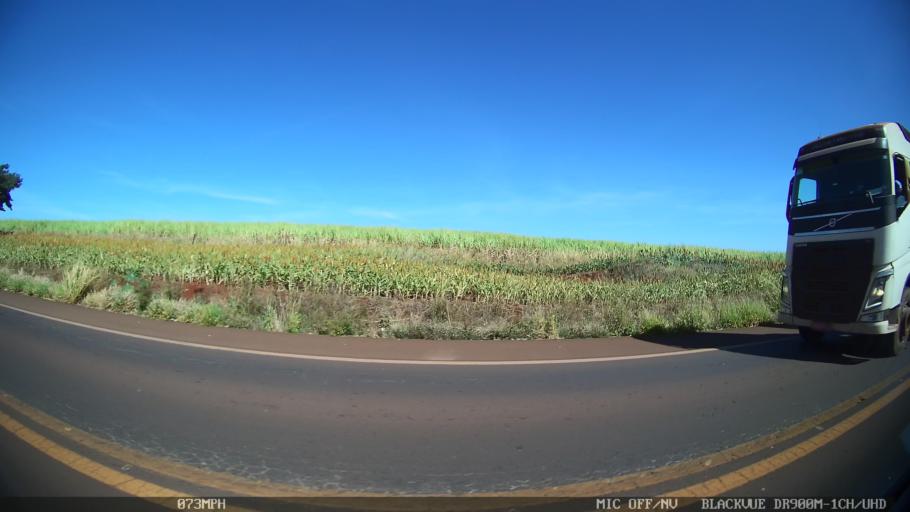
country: BR
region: Sao Paulo
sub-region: Ipua
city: Ipua
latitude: -20.4929
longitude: -48.0480
